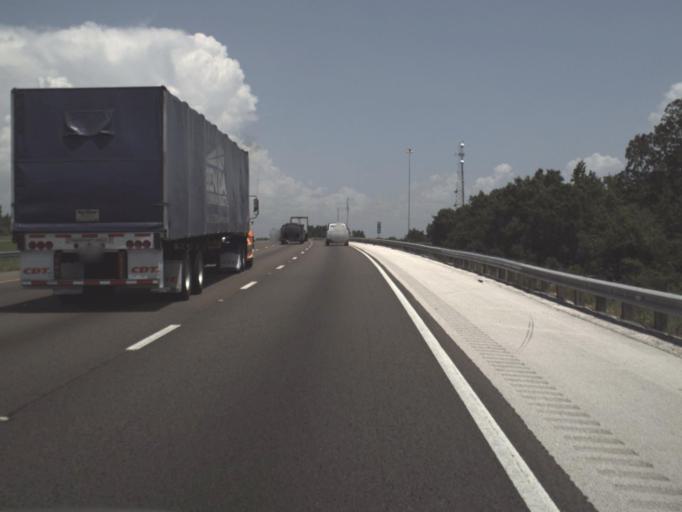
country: US
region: Florida
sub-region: Hillsborough County
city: Sun City Center
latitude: 27.7097
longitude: -82.3861
